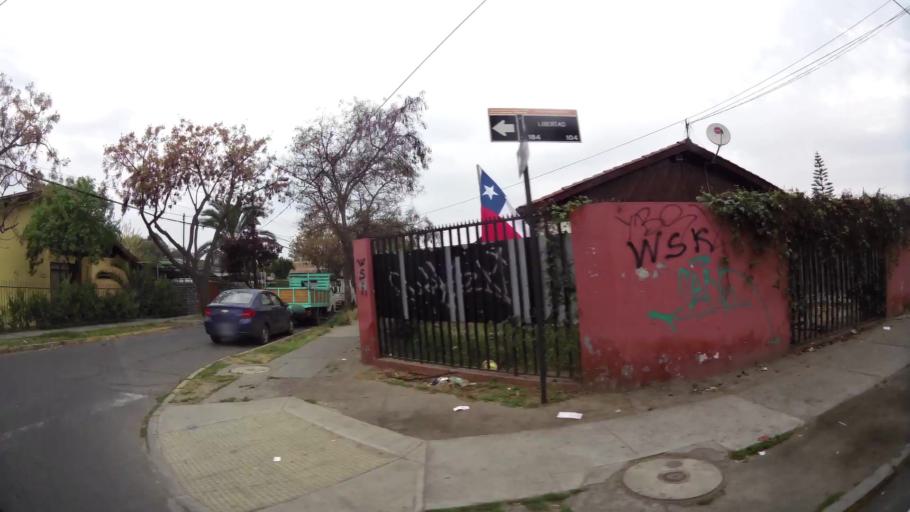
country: CL
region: Santiago Metropolitan
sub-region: Provincia de Santiago
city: Lo Prado
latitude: -33.5056
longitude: -70.7590
